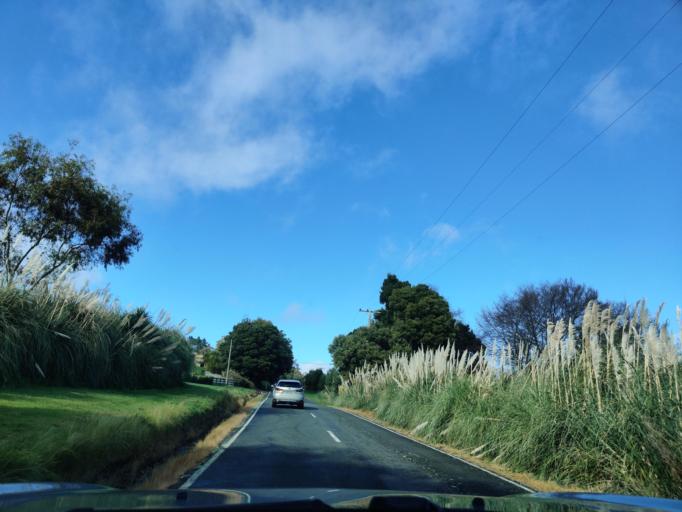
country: NZ
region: Hawke's Bay
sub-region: Hastings District
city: Hastings
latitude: -39.6907
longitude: 176.9005
